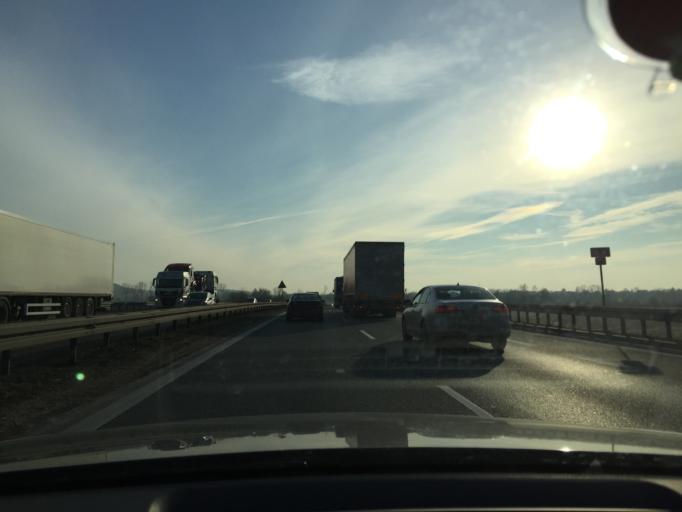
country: PL
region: Lesser Poland Voivodeship
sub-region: Powiat krakowski
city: Balice
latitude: 50.0711
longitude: 19.8104
